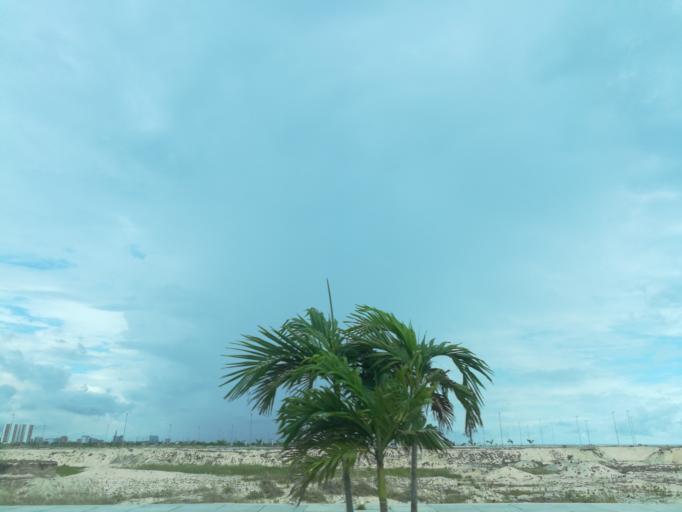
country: NG
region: Lagos
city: Ikoyi
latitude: 6.4048
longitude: 3.4142
